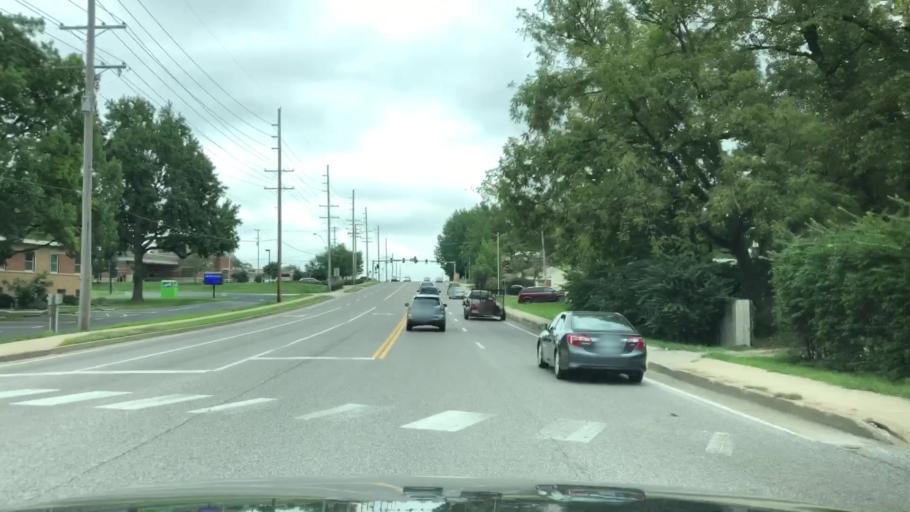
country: US
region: Missouri
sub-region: Saint Louis County
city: Florissant
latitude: 38.7992
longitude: -90.3282
